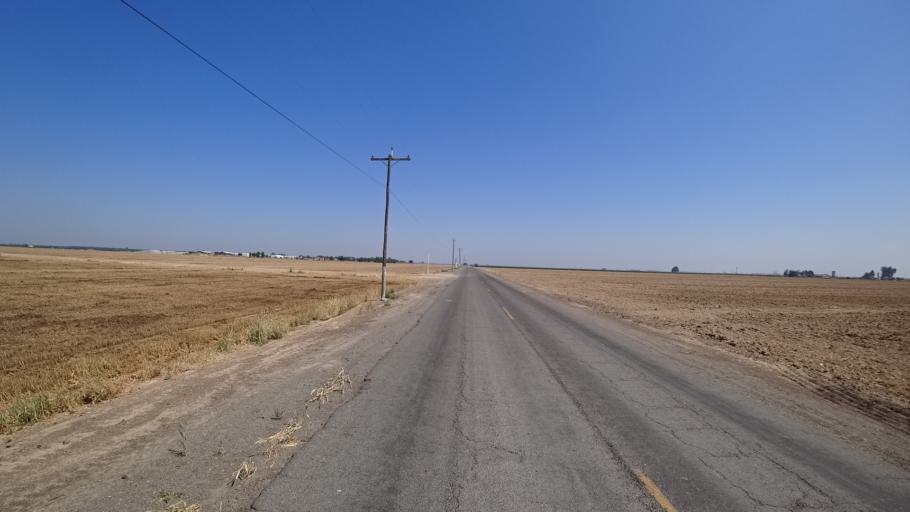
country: US
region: California
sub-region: Tulare County
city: London
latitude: 36.4041
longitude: -119.5288
